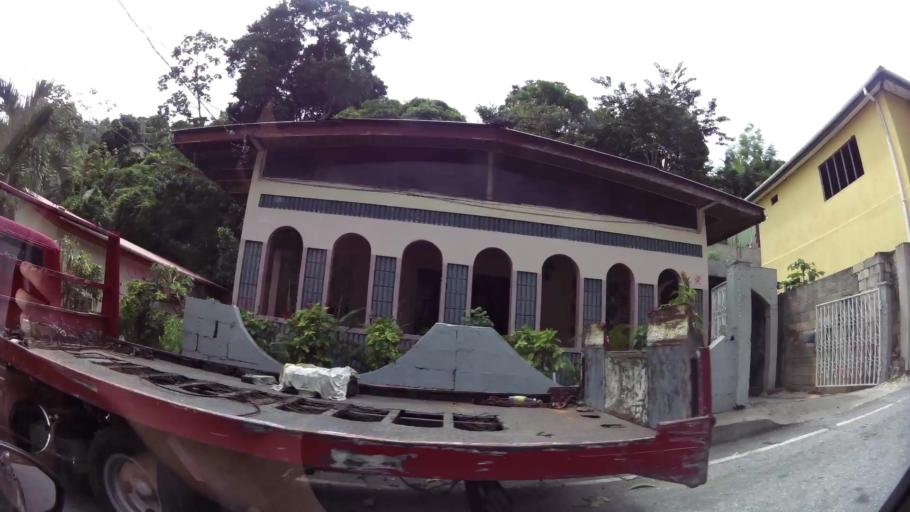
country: TT
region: Diego Martin
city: Petit Valley
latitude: 10.7154
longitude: -61.5279
